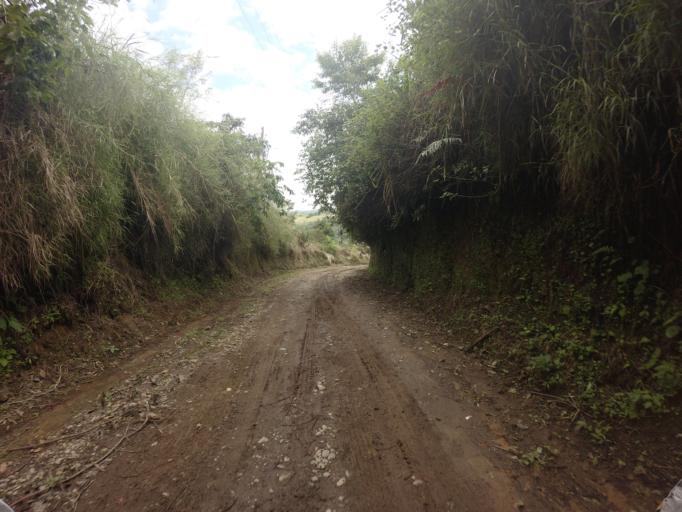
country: CO
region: Valle del Cauca
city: Ulloa
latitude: 4.6973
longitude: -75.7225
